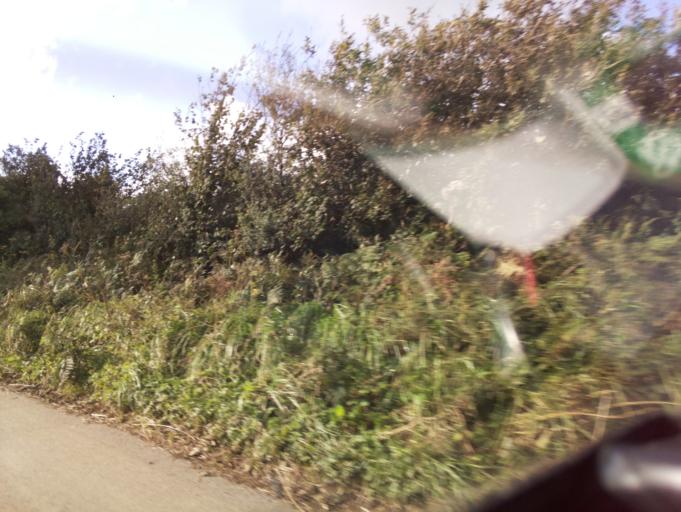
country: GB
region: England
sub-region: Devon
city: Totnes
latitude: 50.3721
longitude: -3.7457
